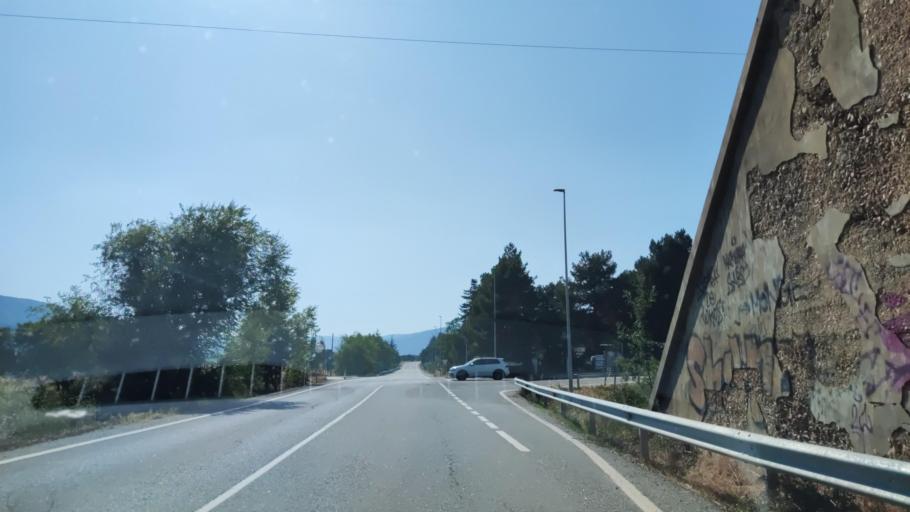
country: ES
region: Madrid
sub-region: Provincia de Madrid
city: Canencia
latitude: 40.9443
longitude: -3.7241
